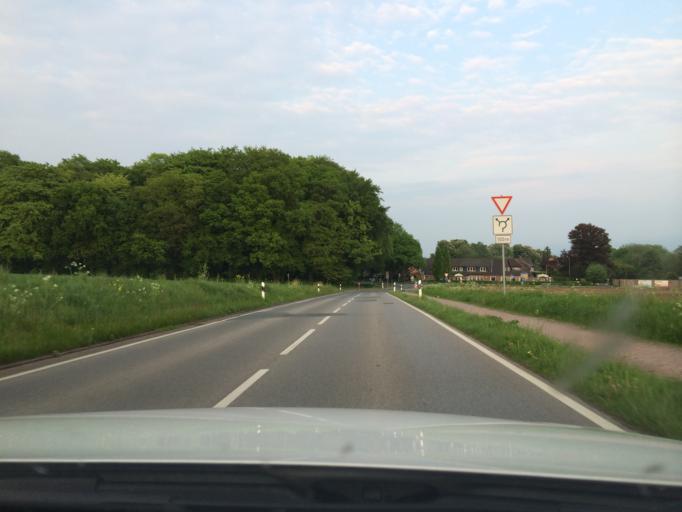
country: DE
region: Lower Saxony
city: Ganderkesee
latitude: 53.0306
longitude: 8.5772
